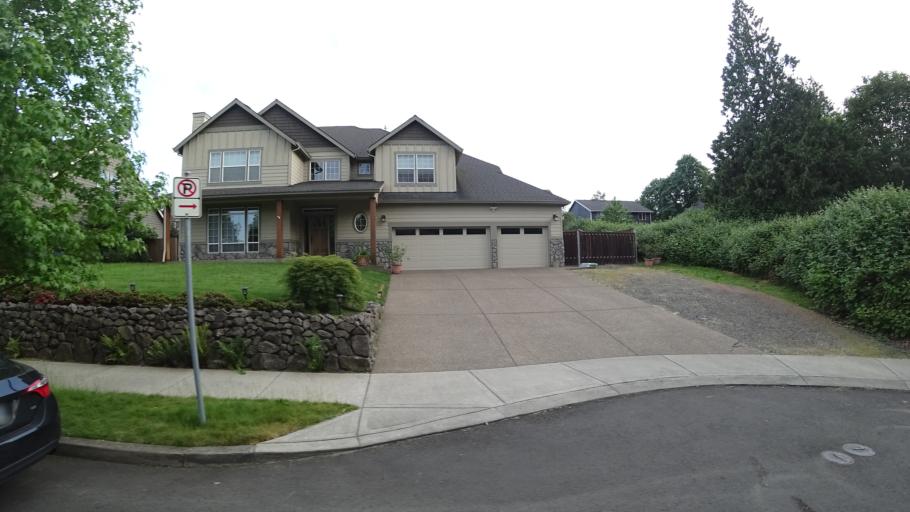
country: US
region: Oregon
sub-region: Clackamas County
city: Happy Valley
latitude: 45.4664
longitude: -122.4996
